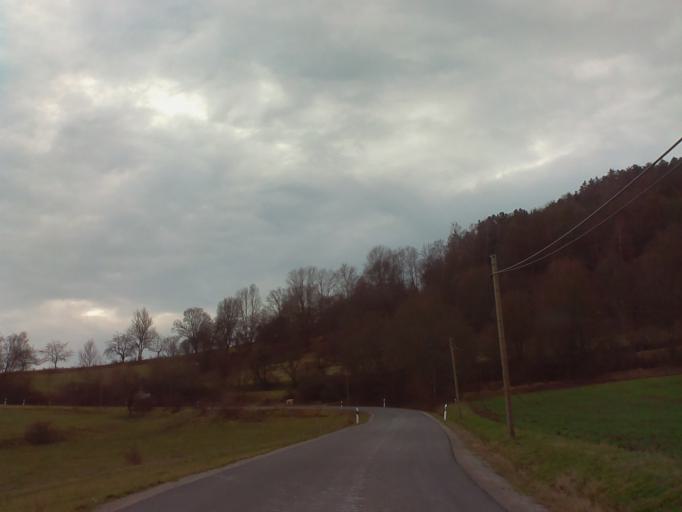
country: DE
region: Thuringia
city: Orlamunde
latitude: 50.7849
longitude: 11.5059
